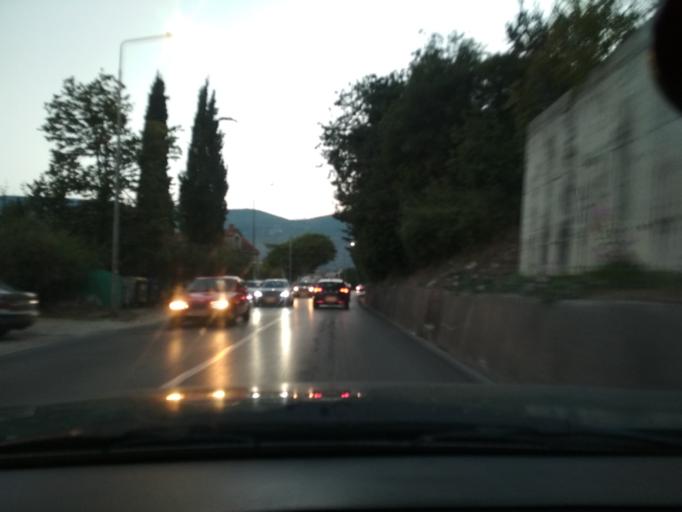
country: ME
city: Igalo
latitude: 42.4617
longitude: 18.5181
